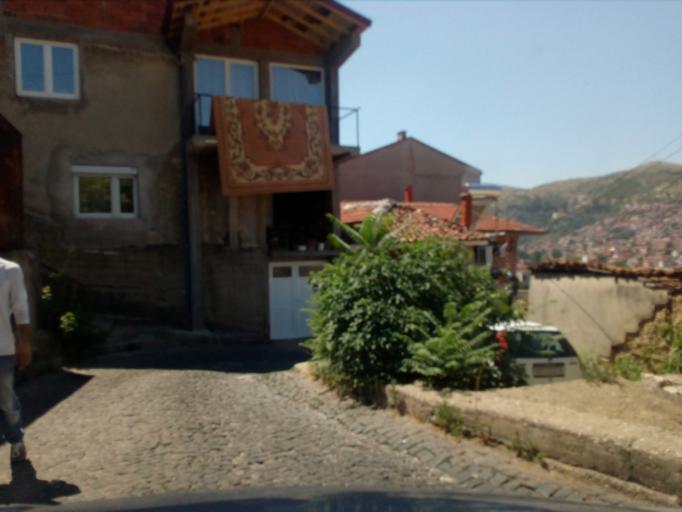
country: MK
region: Veles
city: Veles
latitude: 41.7193
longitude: 21.7896
